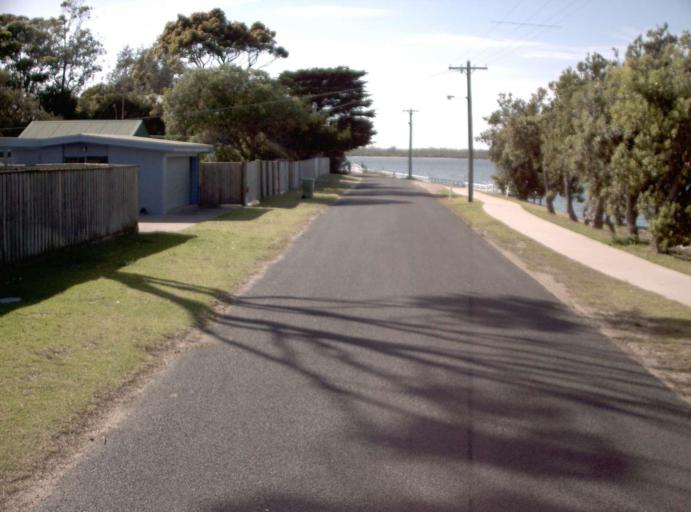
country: AU
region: Victoria
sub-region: East Gippsland
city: Lakes Entrance
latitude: -37.8953
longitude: 147.8547
